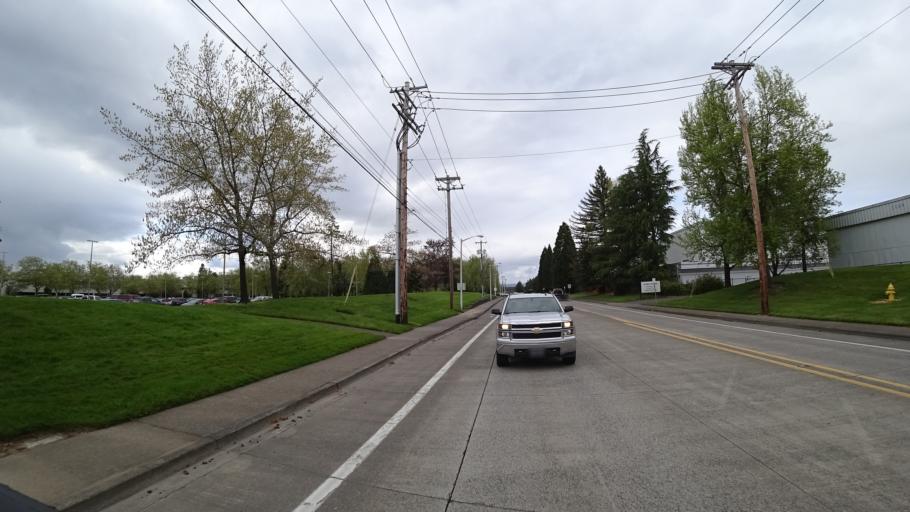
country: US
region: Oregon
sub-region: Washington County
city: Hillsboro
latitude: 45.5406
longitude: -122.9571
